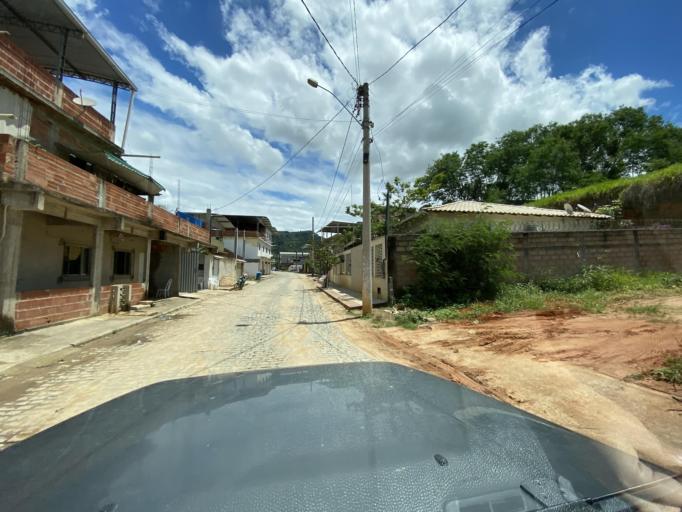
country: BR
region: Espirito Santo
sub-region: Jeronimo Monteiro
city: Jeronimo Monteiro
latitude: -20.7817
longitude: -41.3889
